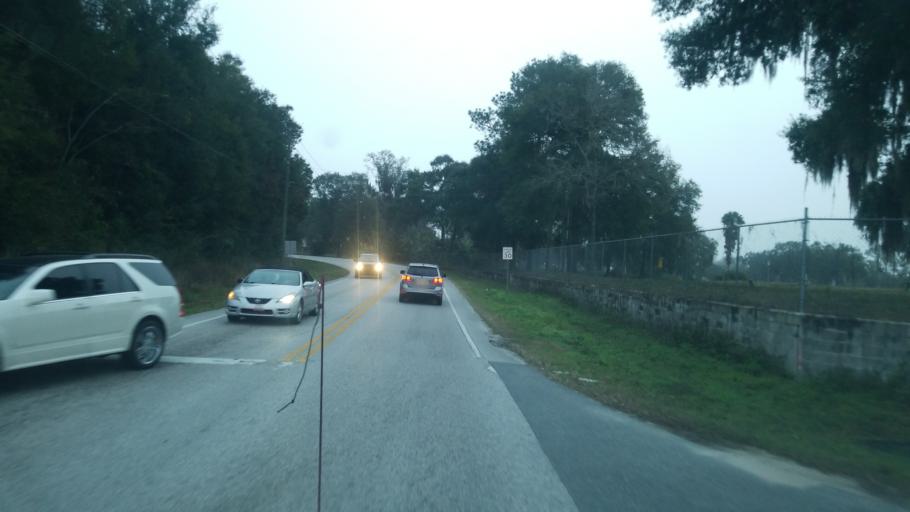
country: US
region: Florida
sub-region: Marion County
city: Ocala
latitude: 29.1481
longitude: -82.1940
